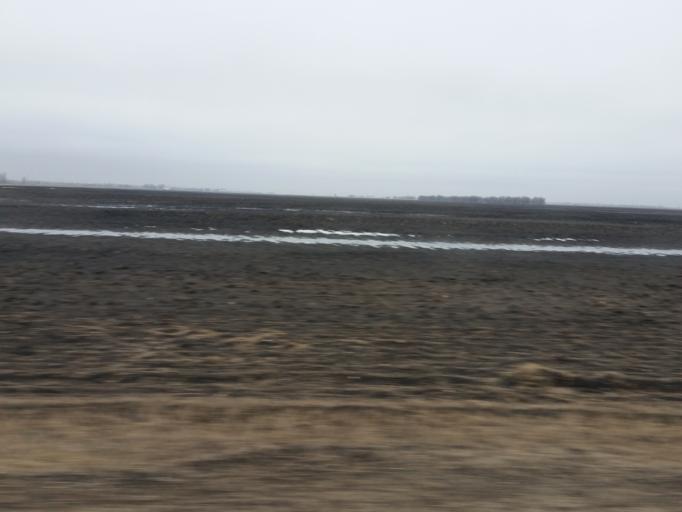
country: US
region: North Dakota
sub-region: Walsh County
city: Grafton
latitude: 48.3618
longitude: -97.1674
